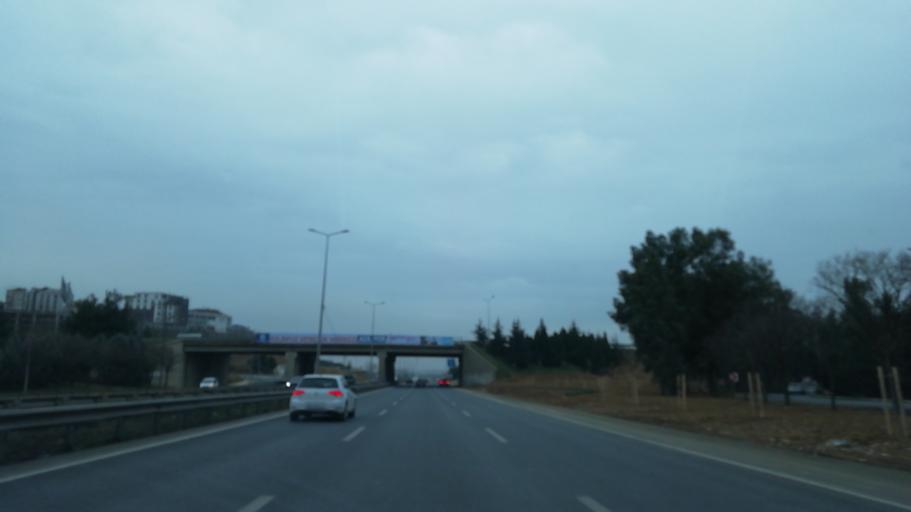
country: TR
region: Kocaeli
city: Darica
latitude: 40.8157
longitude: 29.3631
